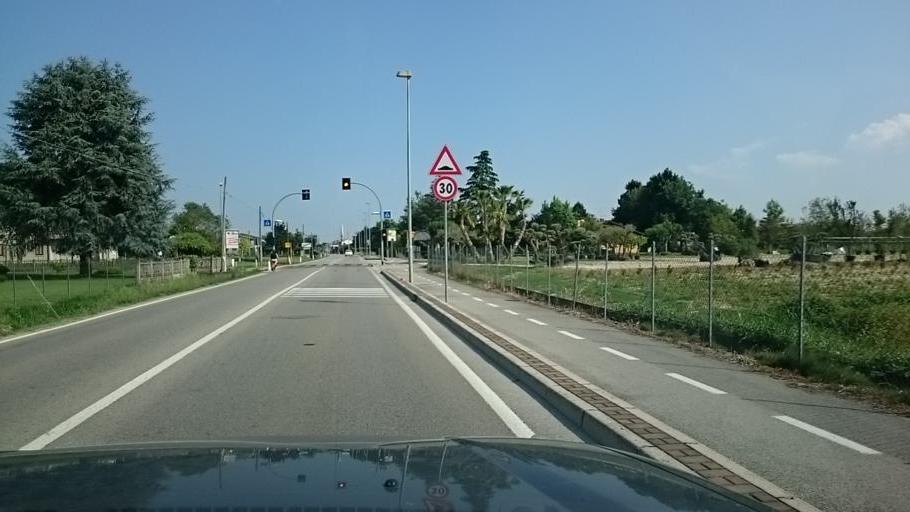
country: IT
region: Veneto
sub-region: Provincia di Padova
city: Saletto
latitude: 45.4685
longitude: 11.8653
